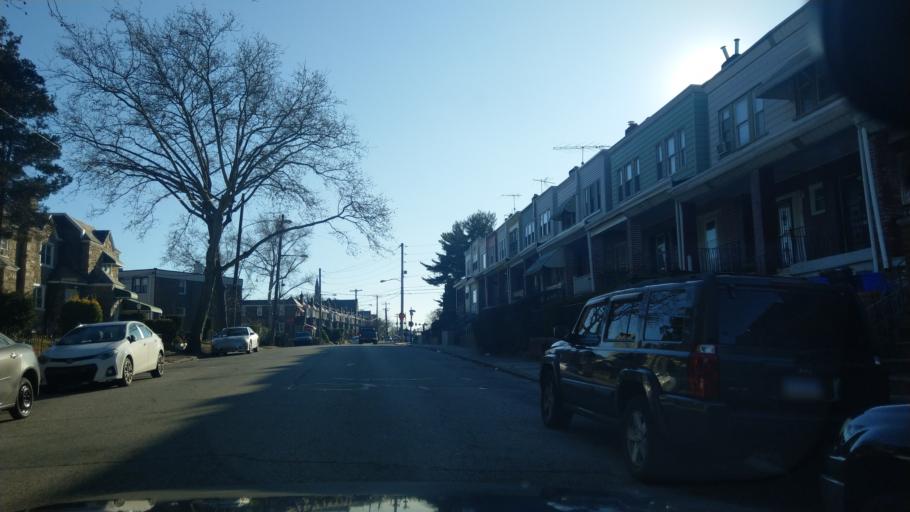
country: US
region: Pennsylvania
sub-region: Montgomery County
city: Wyndmoor
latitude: 40.0419
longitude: -75.1541
